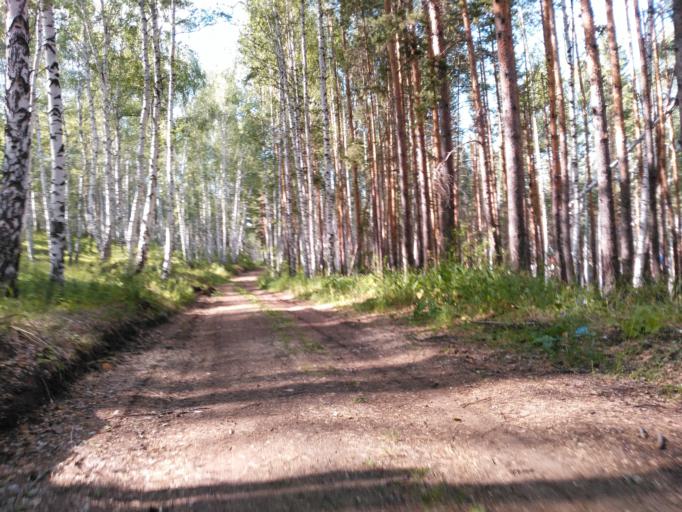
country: RU
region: Bashkortostan
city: Uchaly
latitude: 54.3262
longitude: 59.3614
